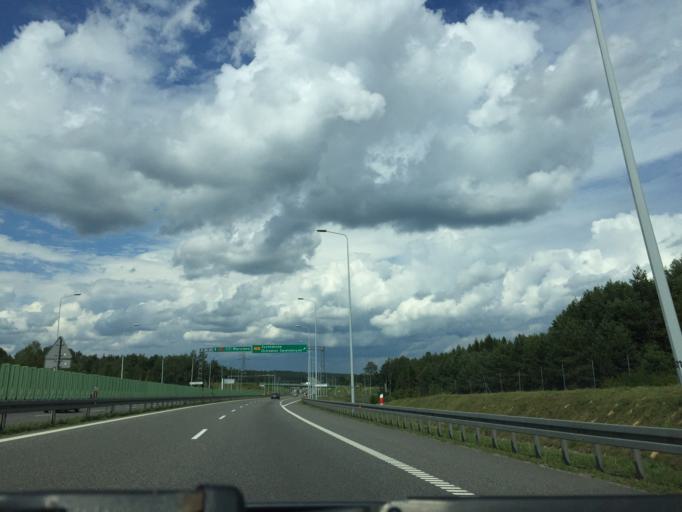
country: PL
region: Swietokrzyskie
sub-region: Powiat skarzyski
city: Suchedniow
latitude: 51.0434
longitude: 20.8188
